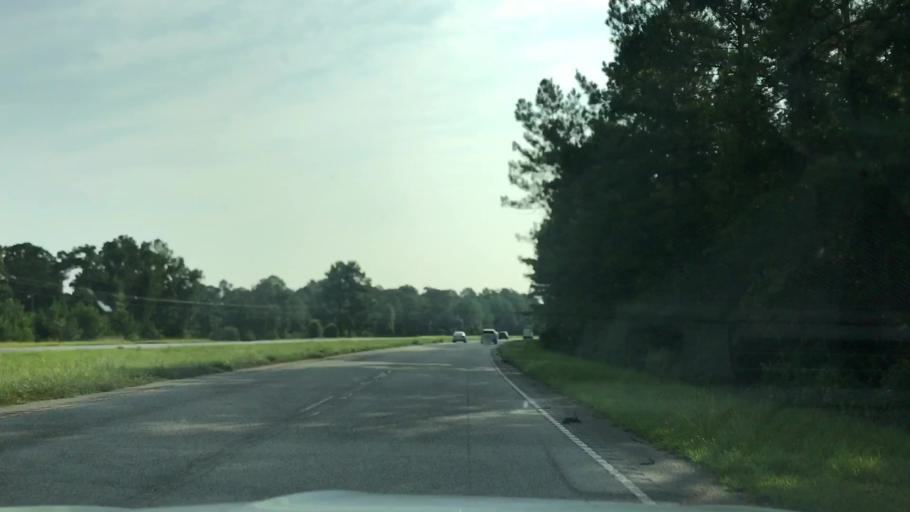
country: US
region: South Carolina
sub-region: Charleston County
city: Awendaw
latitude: 33.0441
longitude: -79.5855
